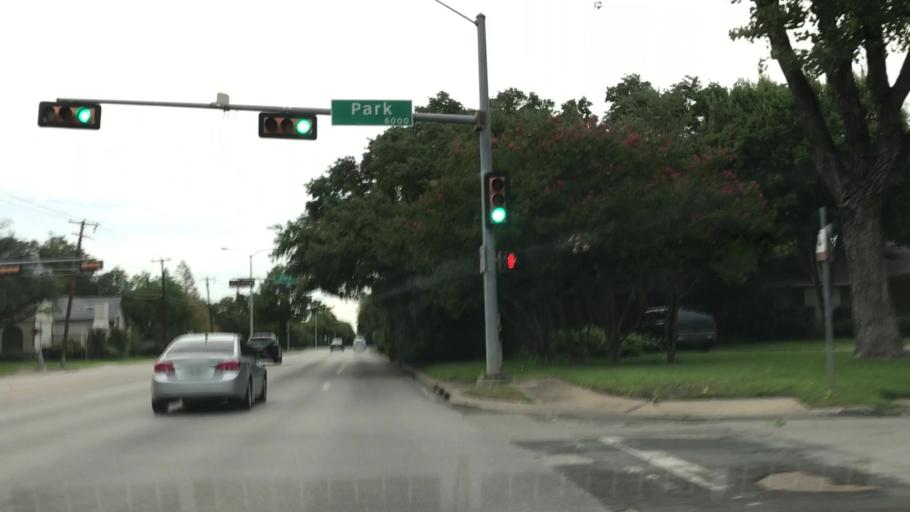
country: US
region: Texas
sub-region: Dallas County
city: University Park
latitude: 32.8734
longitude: -96.8039
